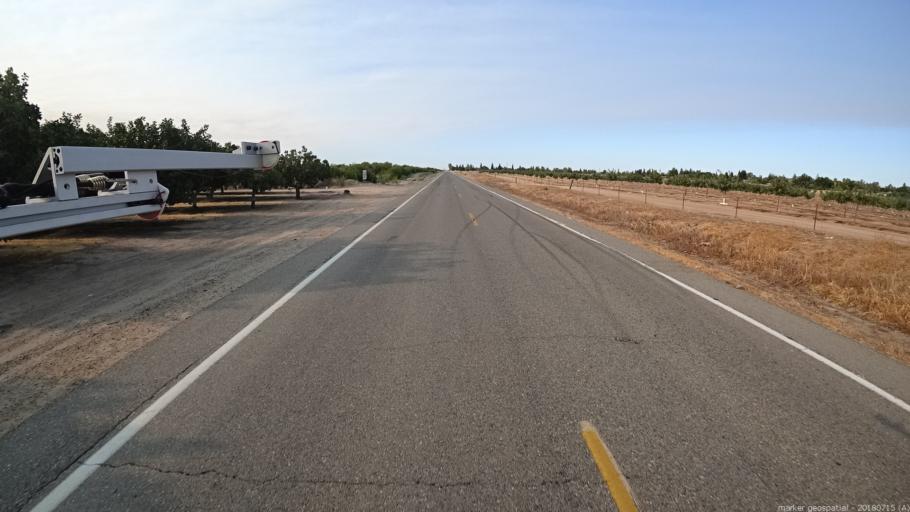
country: US
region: California
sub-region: Madera County
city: Madera Acres
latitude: 37.0329
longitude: -120.0563
